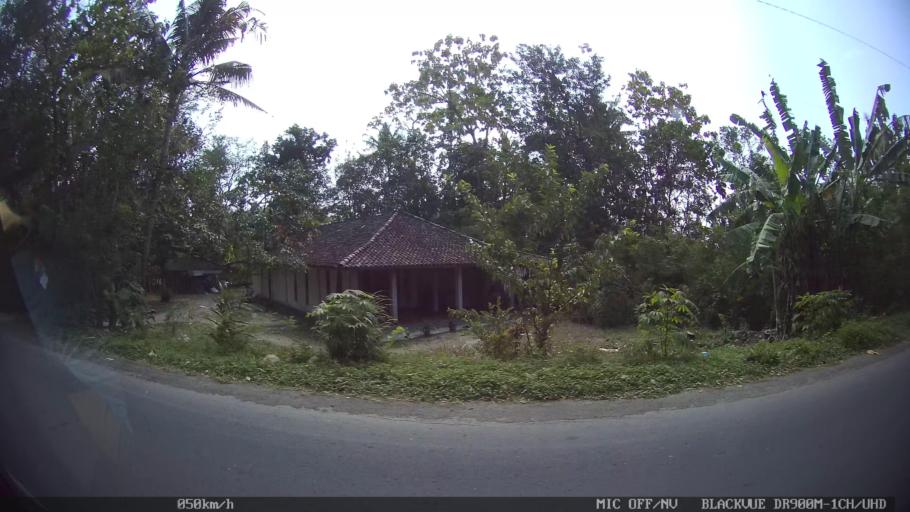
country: ID
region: Daerah Istimewa Yogyakarta
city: Pundong
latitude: -7.9802
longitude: 110.3378
